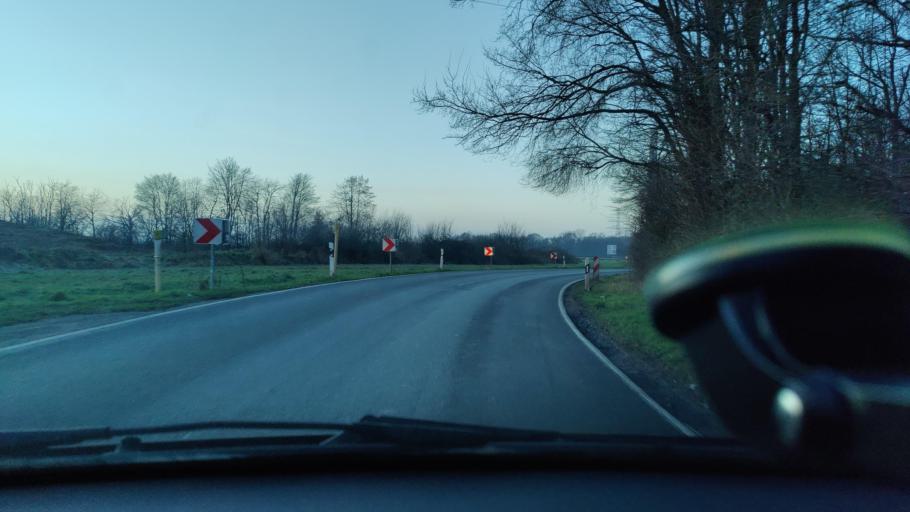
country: DE
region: North Rhine-Westphalia
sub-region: Regierungsbezirk Dusseldorf
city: Voerde
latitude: 51.5692
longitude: 6.6946
